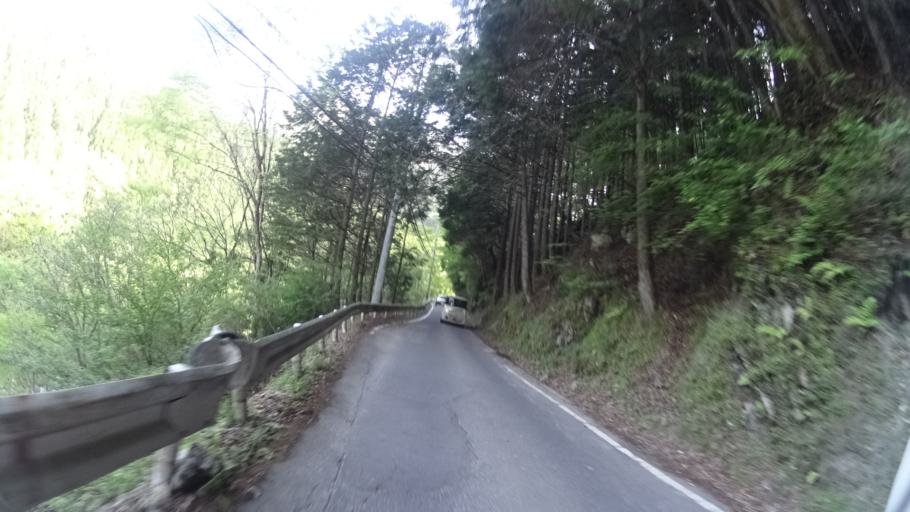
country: JP
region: Tokushima
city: Ikedacho
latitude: 33.8708
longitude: 133.9762
